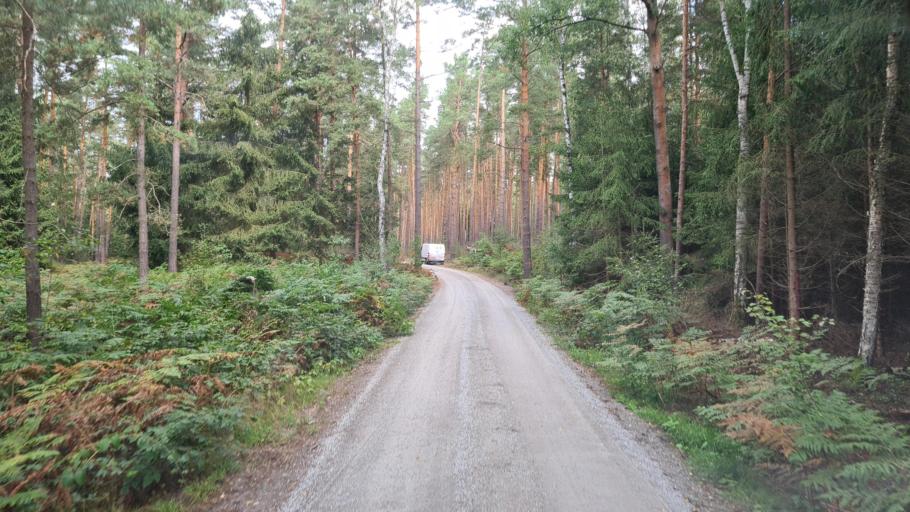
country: DE
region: Brandenburg
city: Schonborn
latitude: 51.6231
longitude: 13.5090
